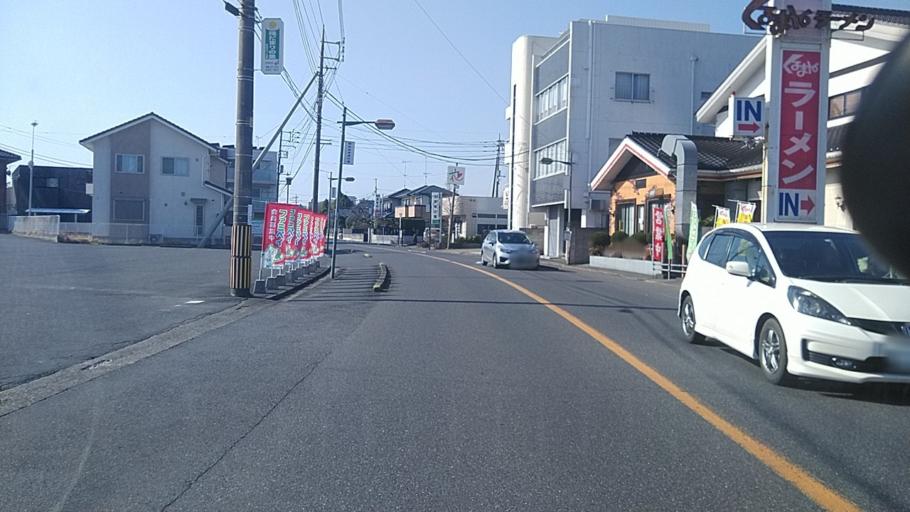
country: JP
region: Chiba
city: Mobara
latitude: 35.4302
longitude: 140.2968
